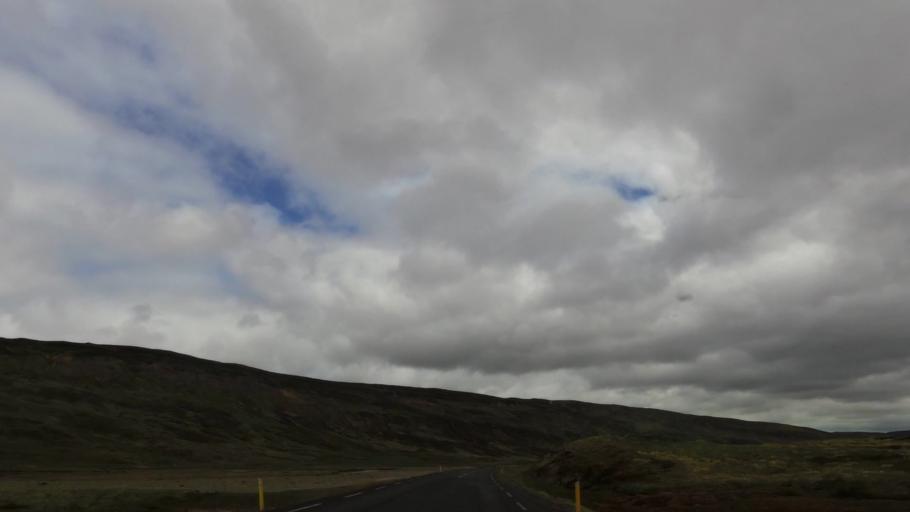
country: IS
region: West
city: Stykkisholmur
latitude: 65.7625
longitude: -21.8401
